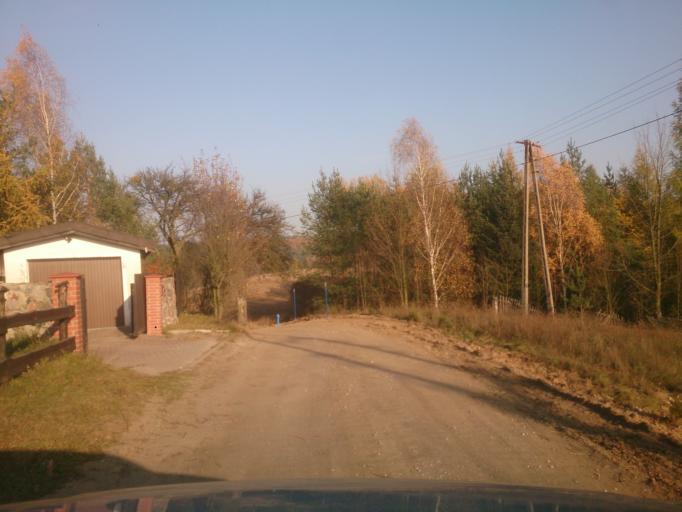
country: PL
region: Kujawsko-Pomorskie
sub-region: Powiat brodnicki
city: Brodnica
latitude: 53.3465
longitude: 19.4474
